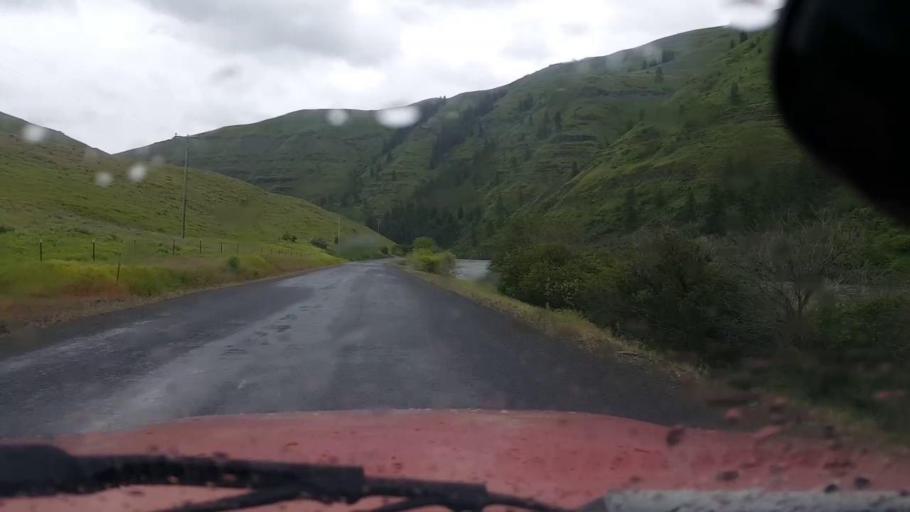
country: US
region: Washington
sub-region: Asotin County
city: Asotin
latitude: 46.0375
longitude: -117.2830
